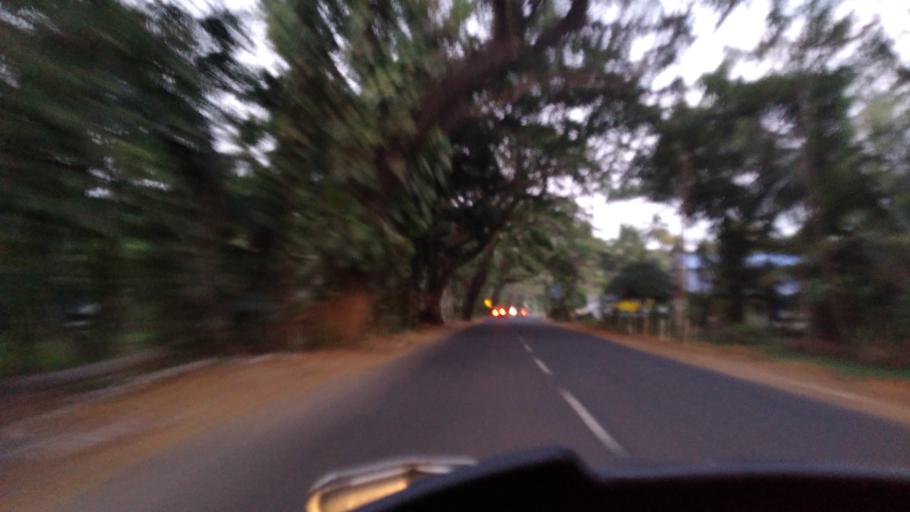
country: IN
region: Kerala
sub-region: Kottayam
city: Kottayam
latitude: 9.6050
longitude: 76.4331
